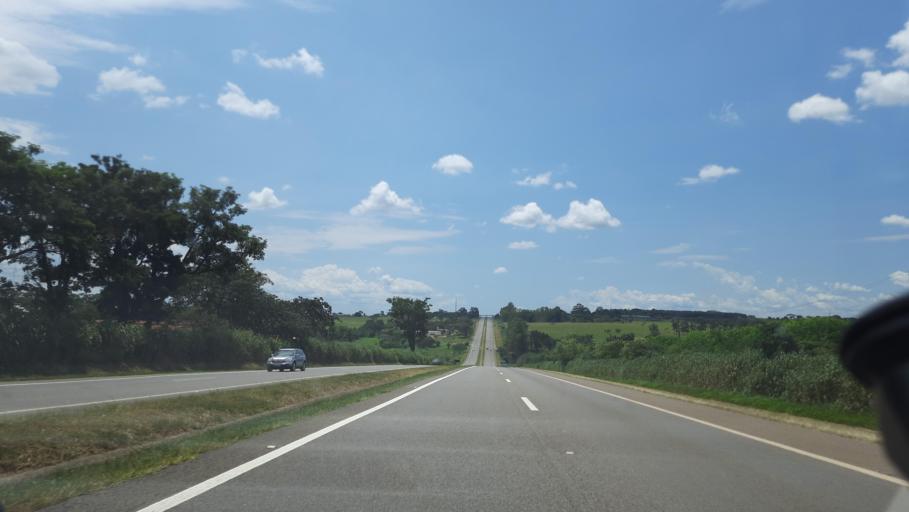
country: BR
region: Sao Paulo
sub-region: Mococa
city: Mococa
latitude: -21.5923
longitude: -47.0396
